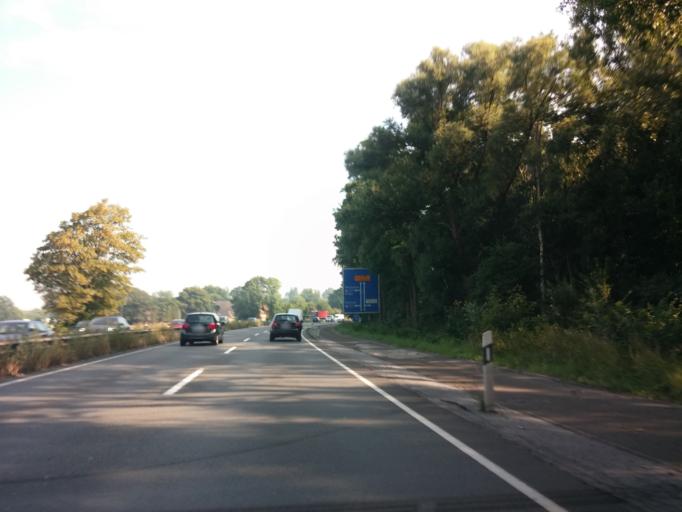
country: DE
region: North Rhine-Westphalia
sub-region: Regierungsbezirk Munster
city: Gladbeck
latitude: 51.5513
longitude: 6.9822
